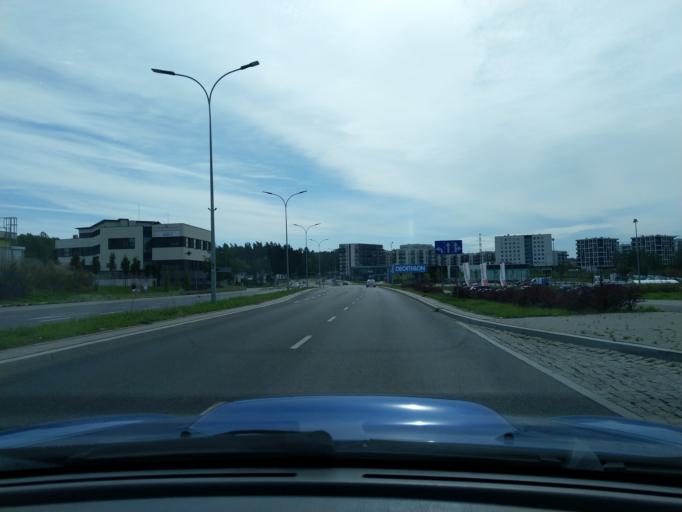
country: PL
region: Warmian-Masurian Voivodeship
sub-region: Olsztyn
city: Kortowo
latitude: 53.7330
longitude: 20.4909
